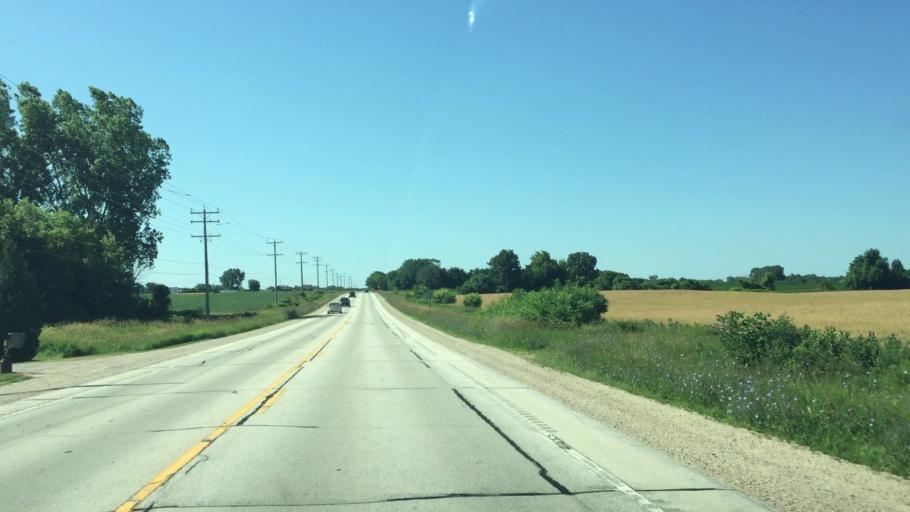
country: US
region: Wisconsin
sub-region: Calumet County
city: Sherwood
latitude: 44.1490
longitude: -88.2648
